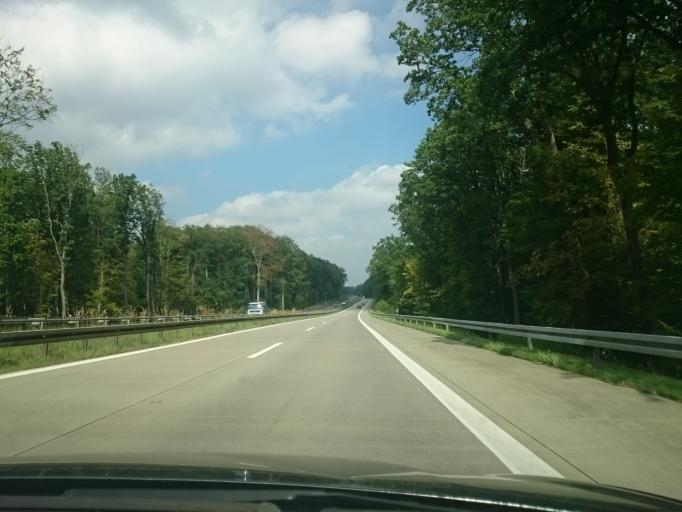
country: DE
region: Brandenburg
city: Althuttendorf
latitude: 52.9908
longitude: 13.8212
